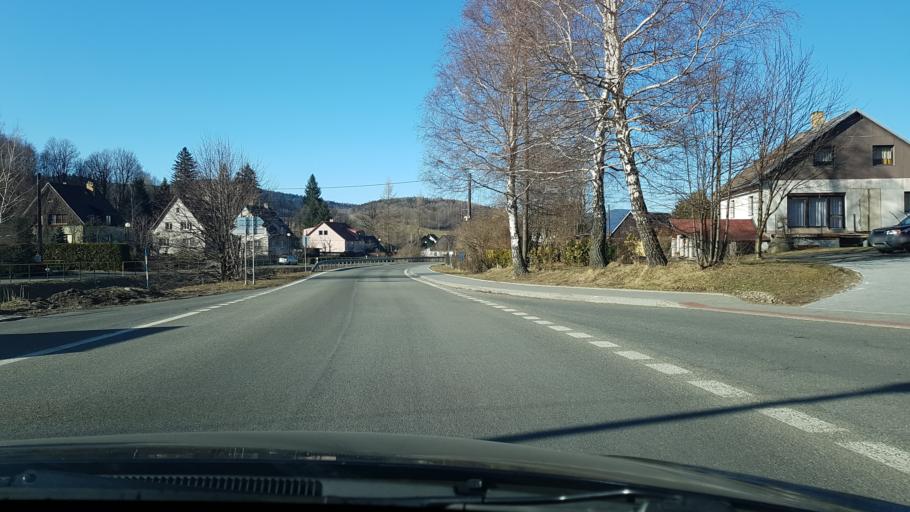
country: CZ
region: Olomoucky
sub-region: Okres Jesenik
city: Jesenik
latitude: 50.1638
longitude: 17.1965
